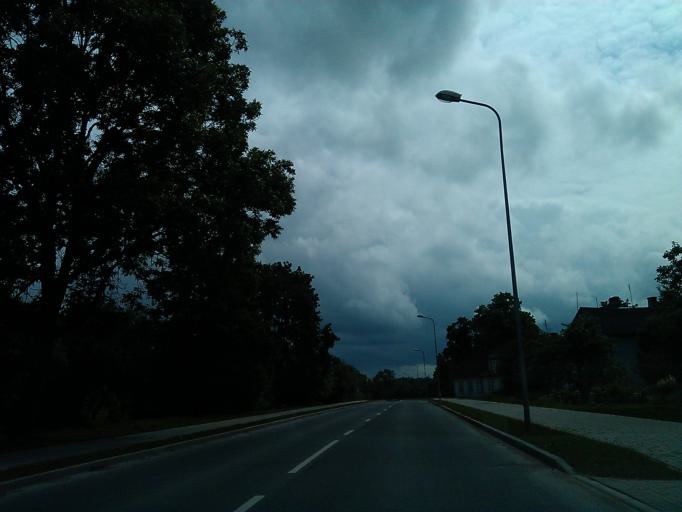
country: LV
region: Aizpute
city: Aizpute
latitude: 56.7148
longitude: 21.6160
